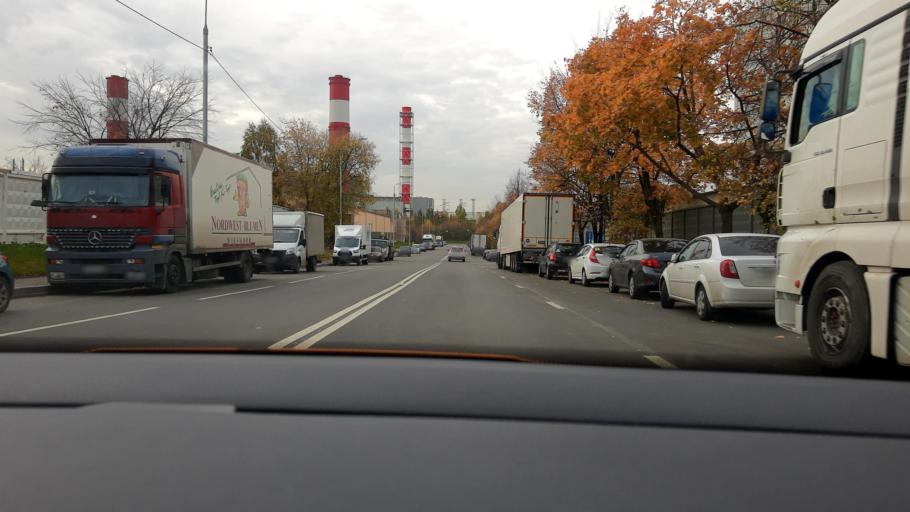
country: RU
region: Moskovskaya
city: Biryulevo Zapadnoye
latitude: 55.5850
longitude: 37.6267
